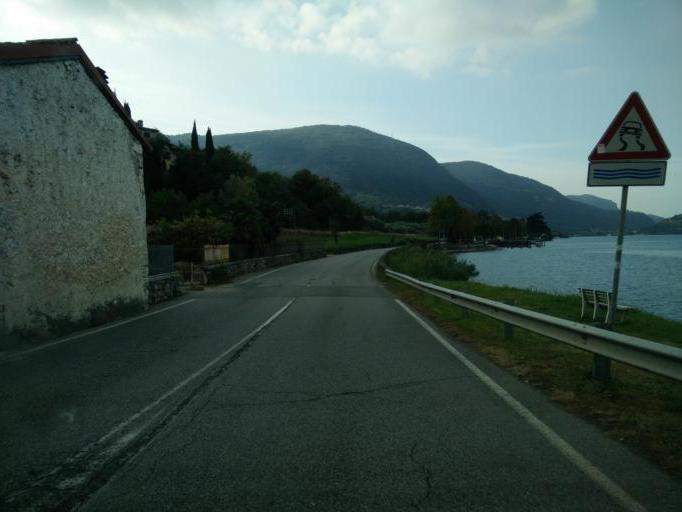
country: IT
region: Lombardy
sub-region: Provincia di Brescia
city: Sale Marasino
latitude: 45.7010
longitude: 10.1081
